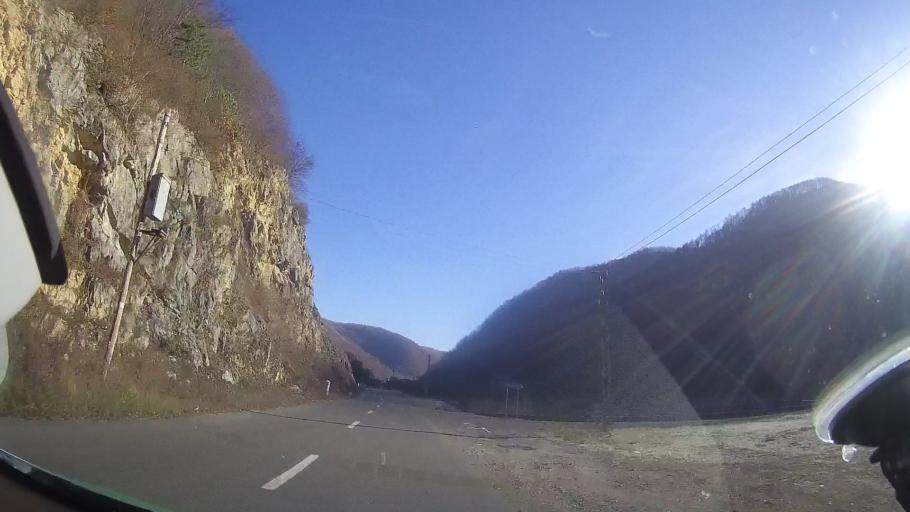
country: RO
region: Bihor
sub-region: Comuna Bulz
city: Bulz
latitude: 46.9158
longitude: 22.6585
